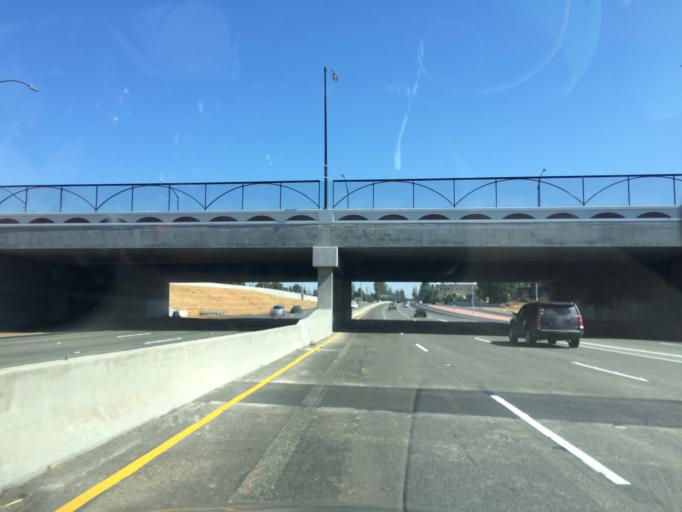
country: US
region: California
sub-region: Santa Clara County
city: Burbank
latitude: 37.3224
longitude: -121.9405
